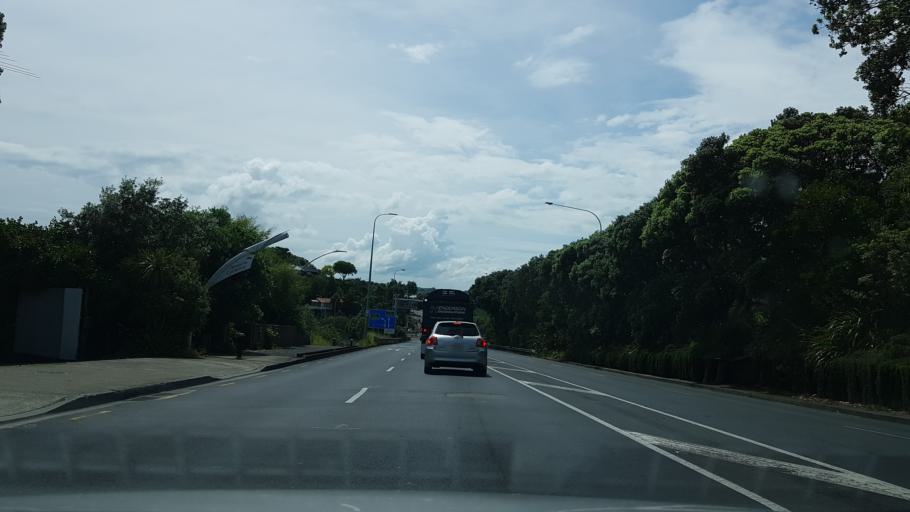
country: NZ
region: Auckland
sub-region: Auckland
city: North Shore
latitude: -36.8122
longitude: 174.7482
